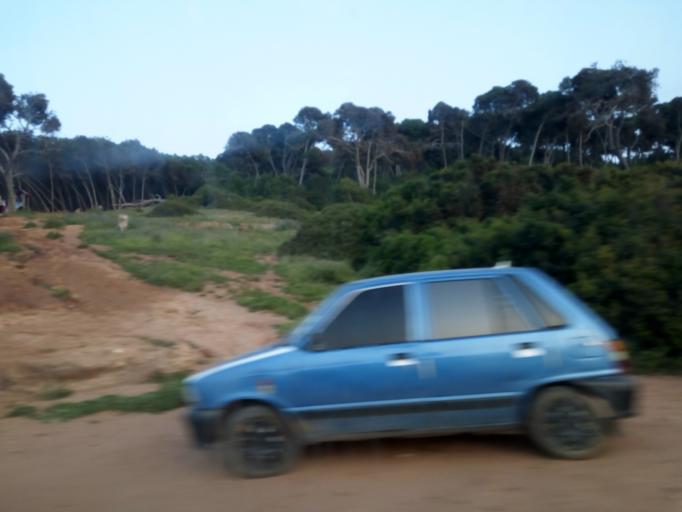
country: DZ
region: Tipaza
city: Bou Ismail
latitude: 36.6194
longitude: 2.6490
